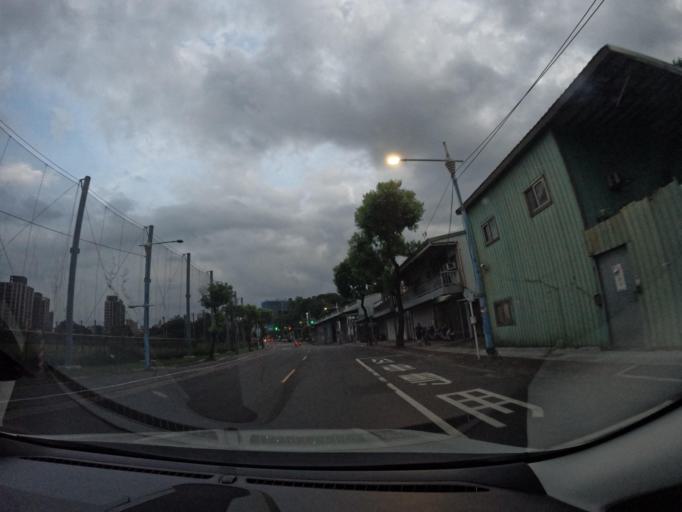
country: TW
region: Taipei
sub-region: Taipei
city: Banqiao
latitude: 24.9785
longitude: 121.4543
